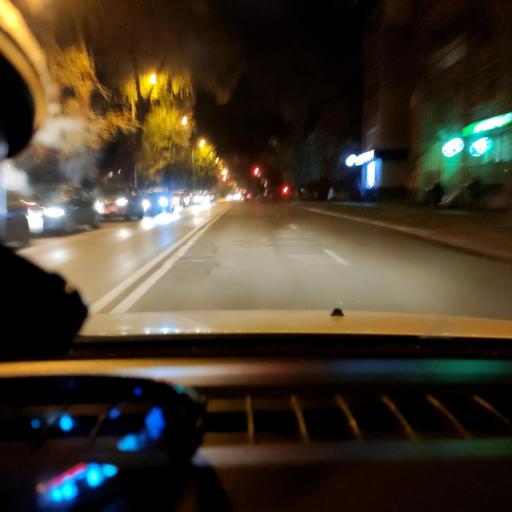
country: RU
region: Samara
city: Samara
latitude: 53.1969
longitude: 50.1352
